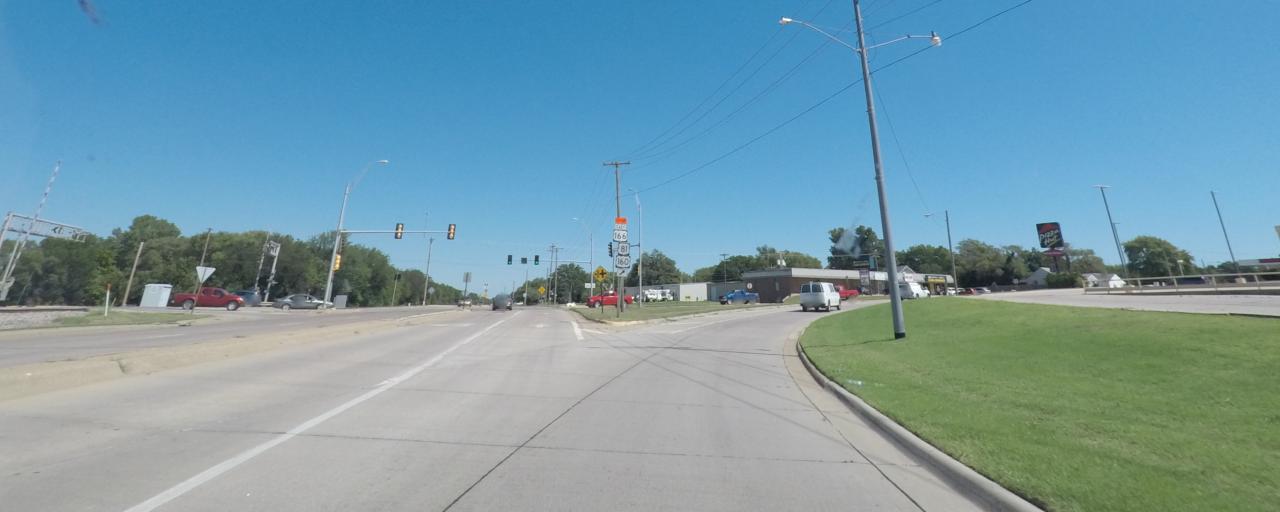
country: US
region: Kansas
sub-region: Sumner County
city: Wellington
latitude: 37.2737
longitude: -97.4017
